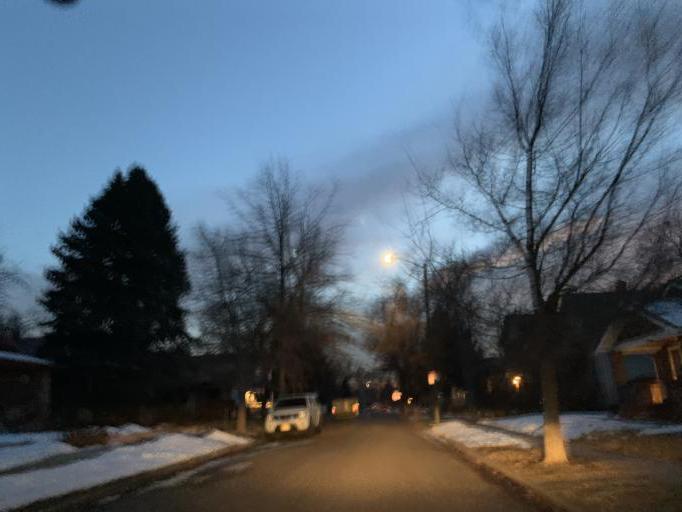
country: US
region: Colorado
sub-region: Jefferson County
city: Edgewater
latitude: 39.7736
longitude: -105.0405
